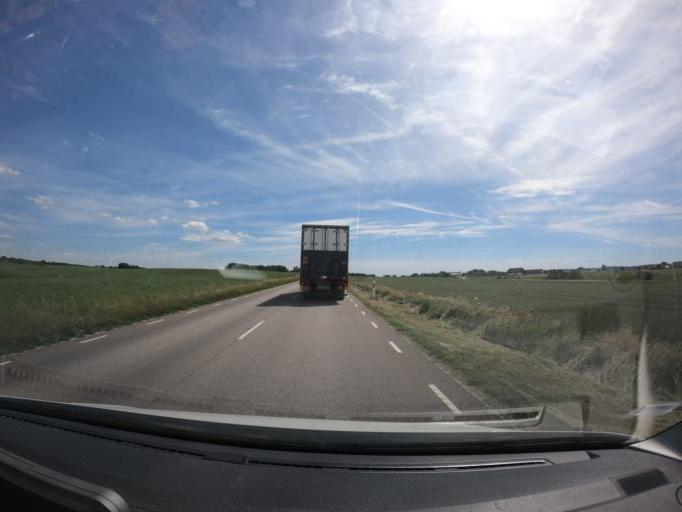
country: SE
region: Skane
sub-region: Astorps Kommun
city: Kvidinge
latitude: 56.1581
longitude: 13.0920
